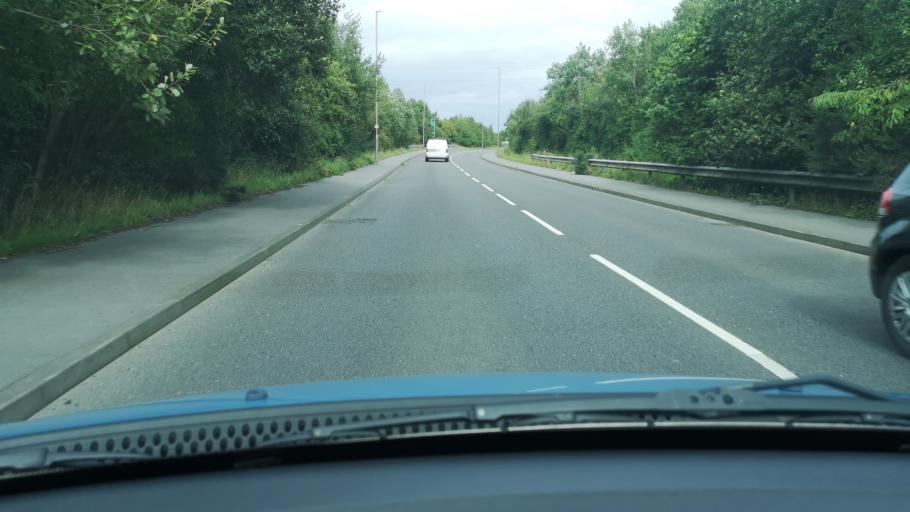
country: GB
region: England
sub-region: Barnsley
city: Shafton
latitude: 53.5887
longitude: -1.4017
